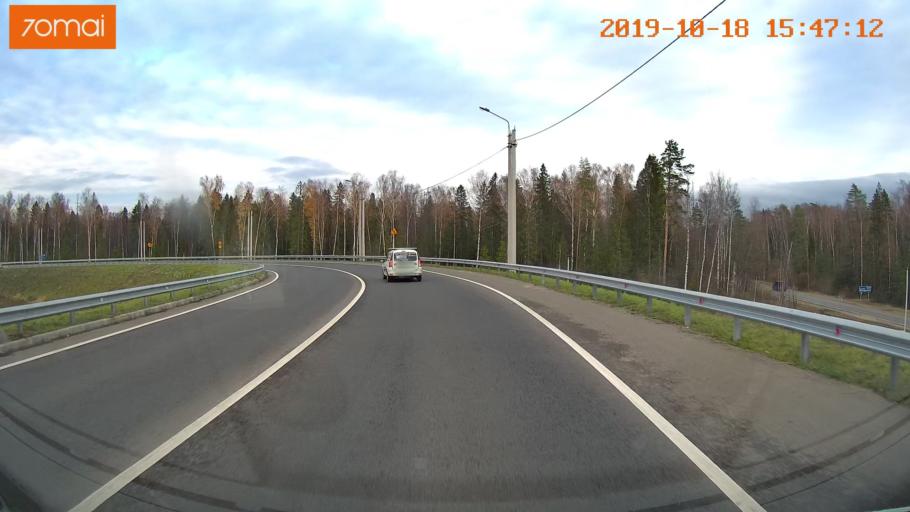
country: RU
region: Vladimir
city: Golovino
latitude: 56.0160
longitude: 40.5770
